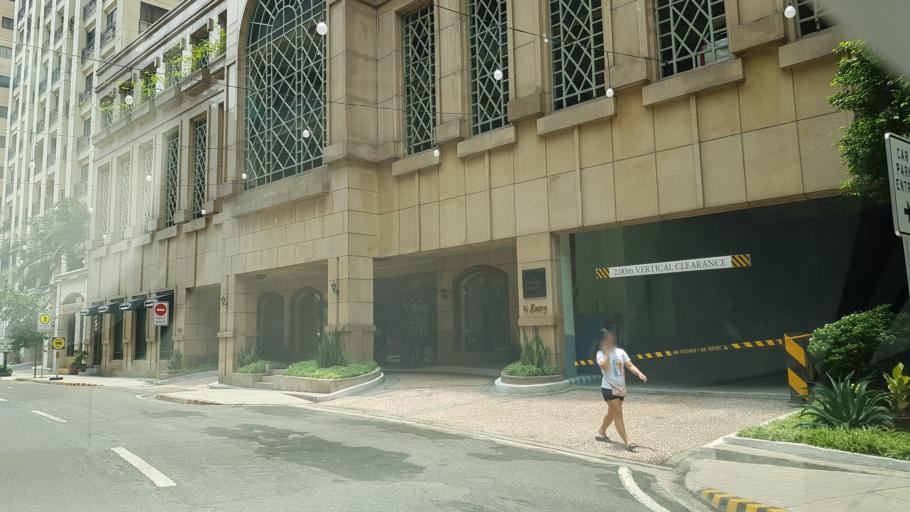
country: PH
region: Metro Manila
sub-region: Marikina
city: Calumpang
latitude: 14.6097
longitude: 121.0791
